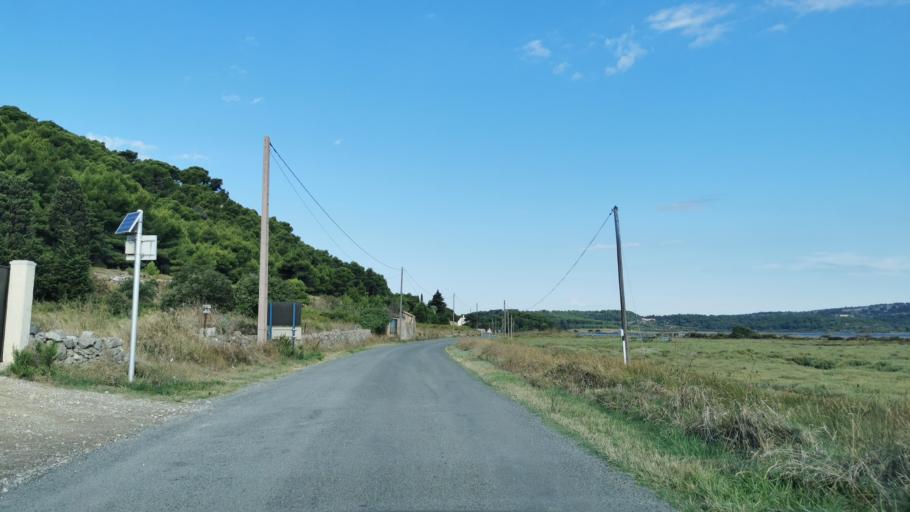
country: FR
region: Languedoc-Roussillon
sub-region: Departement de l'Aude
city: Gruissan
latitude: 43.1042
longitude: 3.0825
